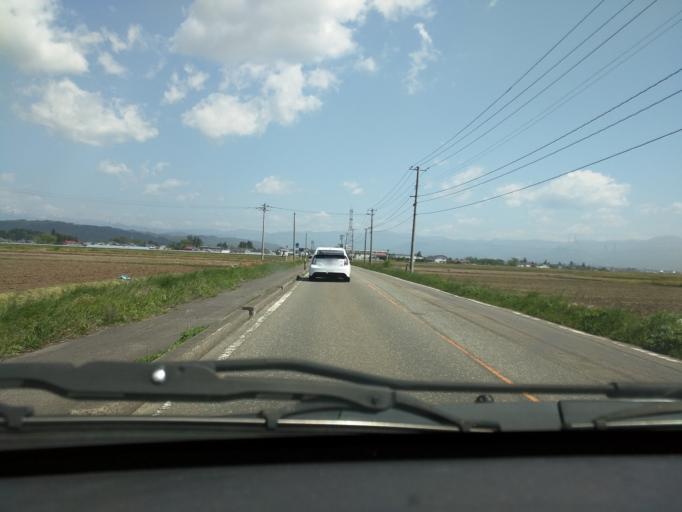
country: JP
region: Fukushima
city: Kitakata
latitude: 37.5808
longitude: 139.8338
